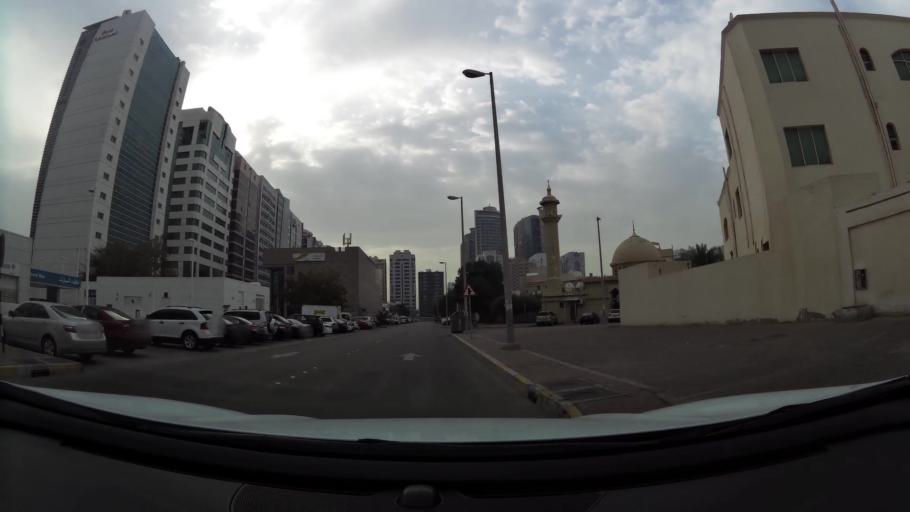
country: AE
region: Abu Dhabi
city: Abu Dhabi
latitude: 24.4763
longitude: 54.3712
